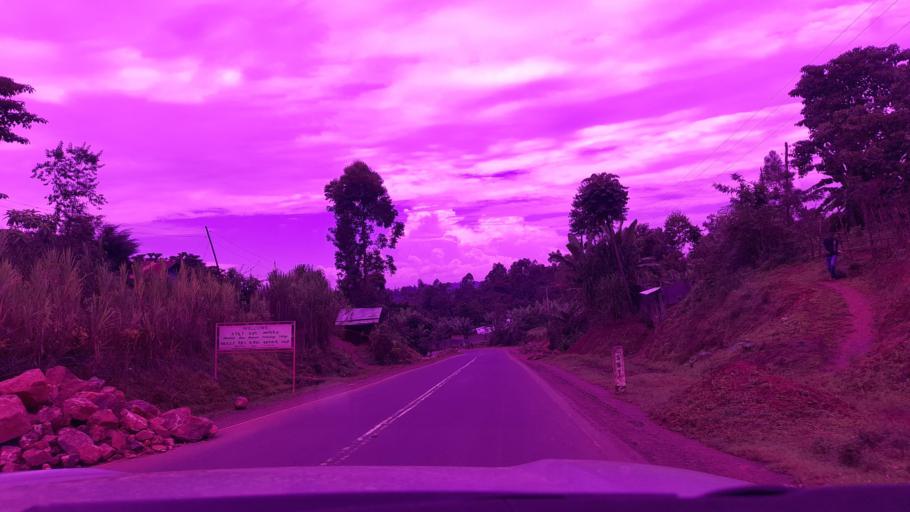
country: ET
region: Southern Nations, Nationalities, and People's Region
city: Mizan Teferi
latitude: 7.0053
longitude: 35.6073
